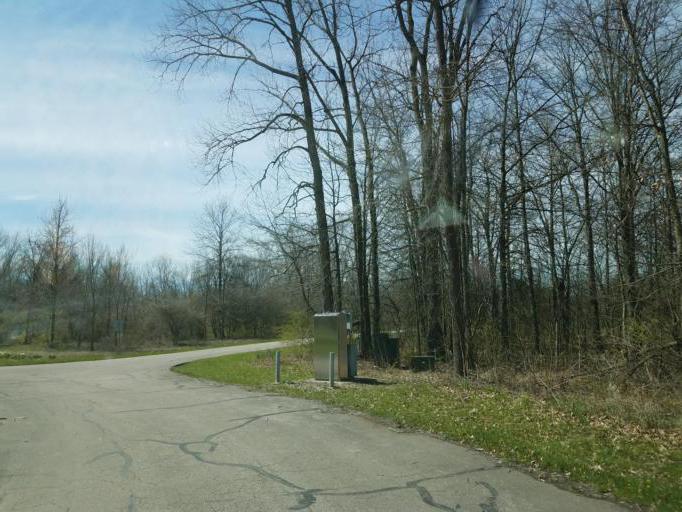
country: US
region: Ohio
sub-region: Delaware County
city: Delaware
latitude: 40.3976
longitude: -83.0602
